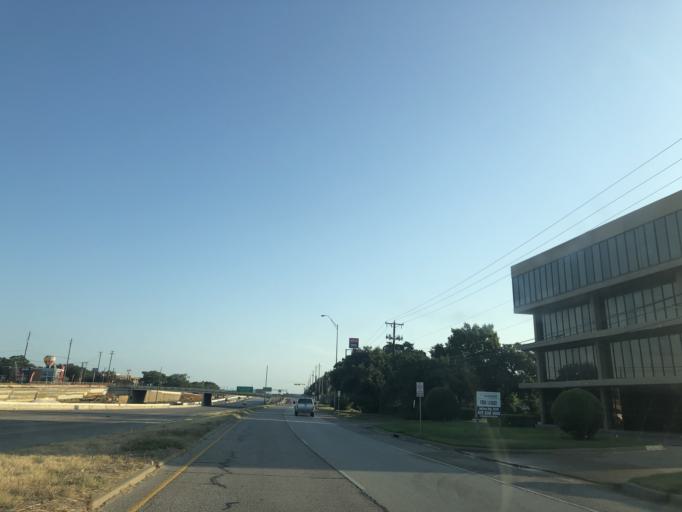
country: US
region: Texas
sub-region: Tarrant County
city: Arlington
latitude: 32.7646
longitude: -97.0629
